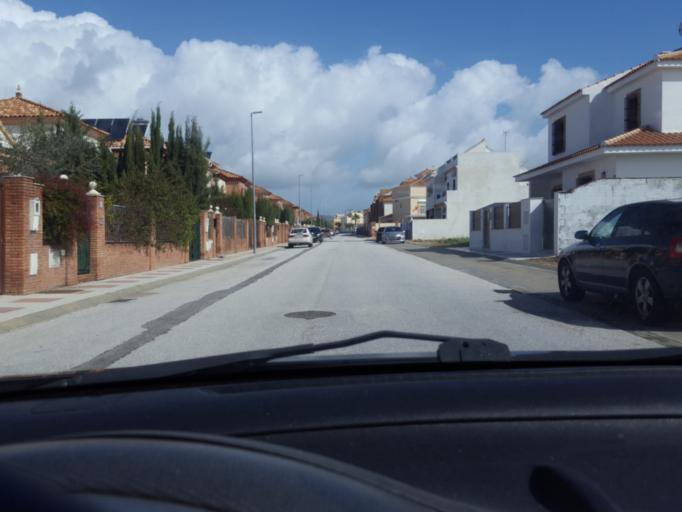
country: ES
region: Andalusia
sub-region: Provincia de Sevilla
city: Acala del Rio
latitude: 37.5172
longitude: -5.9872
